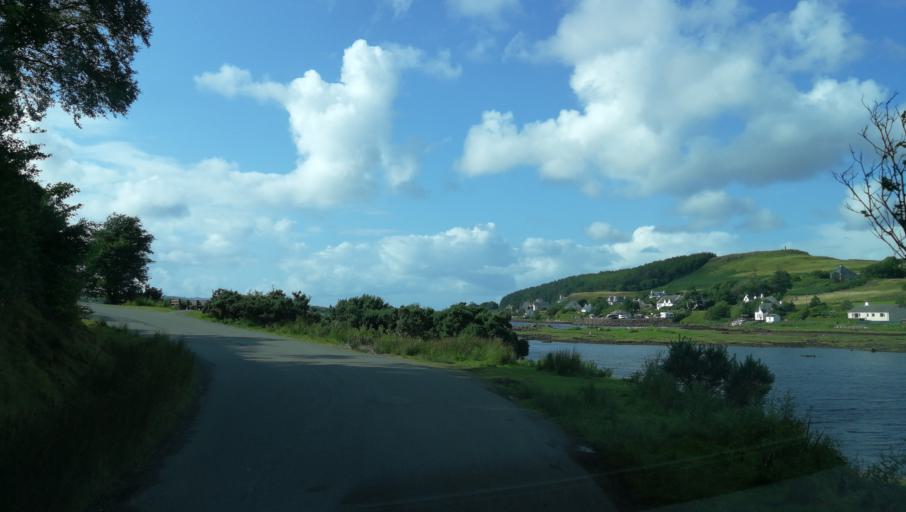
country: GB
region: Scotland
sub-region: Highland
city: Isle of Skye
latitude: 57.4315
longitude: -6.5765
